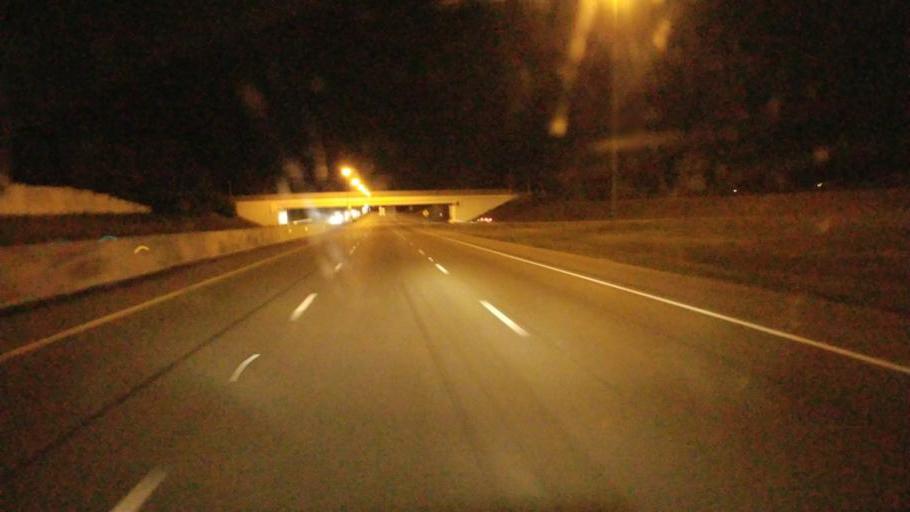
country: US
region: Ohio
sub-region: Montgomery County
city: Vandalia
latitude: 39.8646
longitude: -84.2242
